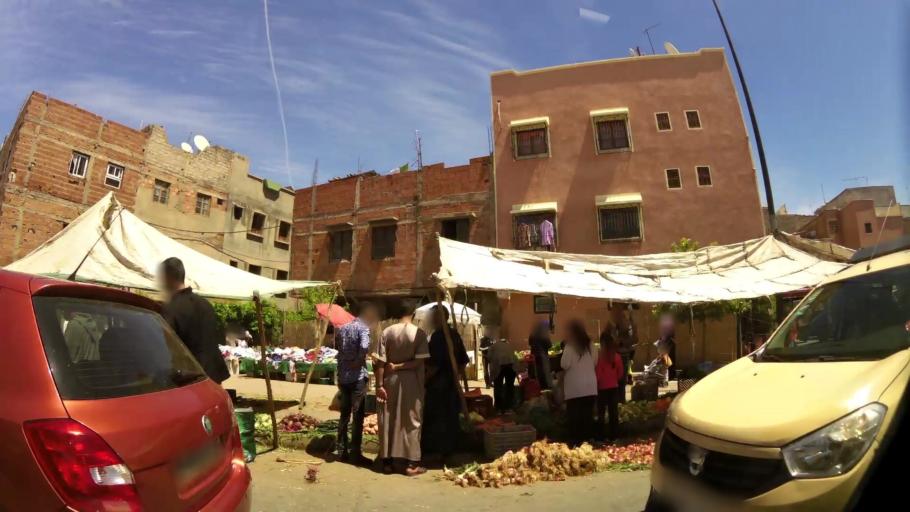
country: MA
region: Marrakech-Tensift-Al Haouz
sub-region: Marrakech
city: Marrakesh
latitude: 31.6541
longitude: -7.9955
